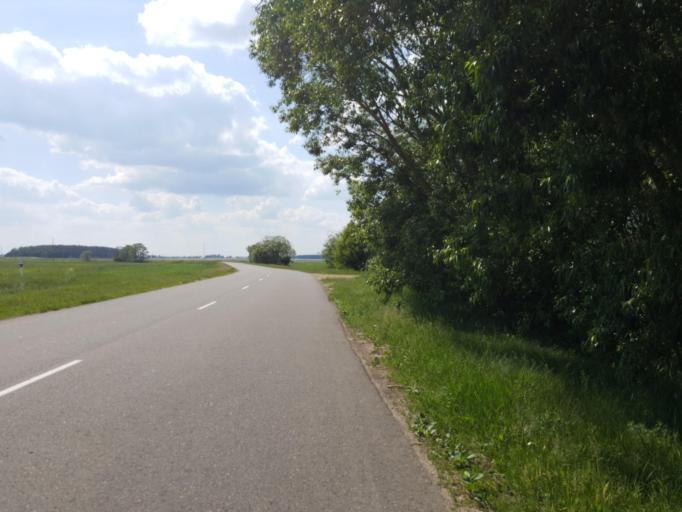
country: BY
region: Brest
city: Kamyanyuki
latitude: 52.5059
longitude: 23.6345
